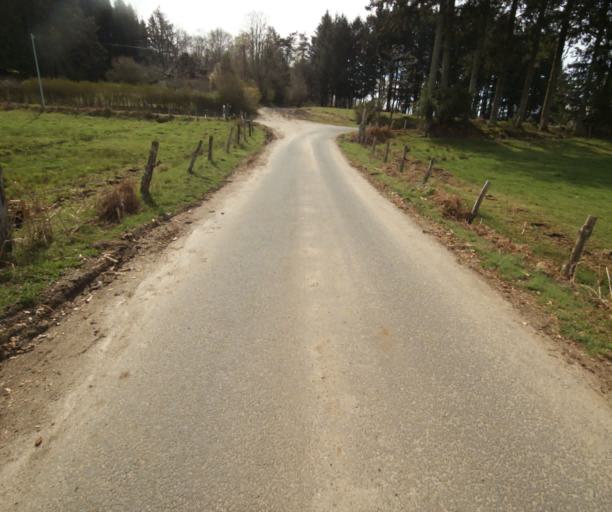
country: FR
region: Limousin
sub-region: Departement de la Correze
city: Correze
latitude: 45.3498
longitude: 1.8972
